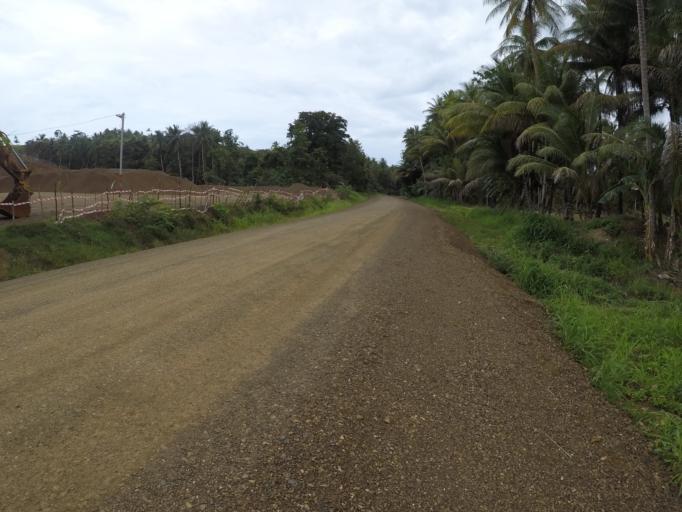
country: PG
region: Milne Bay
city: Alotau
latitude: -10.2624
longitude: 150.8105
